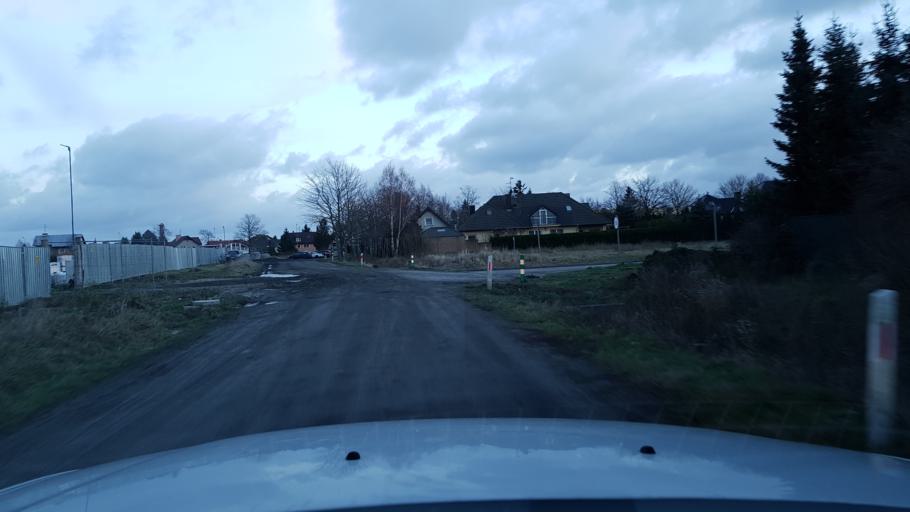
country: PL
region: West Pomeranian Voivodeship
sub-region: Powiat kolobrzeski
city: Kolobrzeg
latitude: 54.1505
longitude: 15.5577
